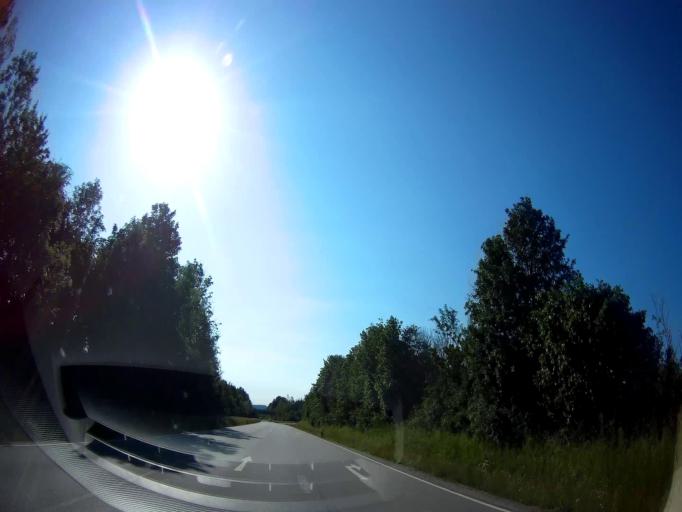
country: DE
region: Bavaria
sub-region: Upper Bavaria
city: Haiming
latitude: 48.2392
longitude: 12.9061
